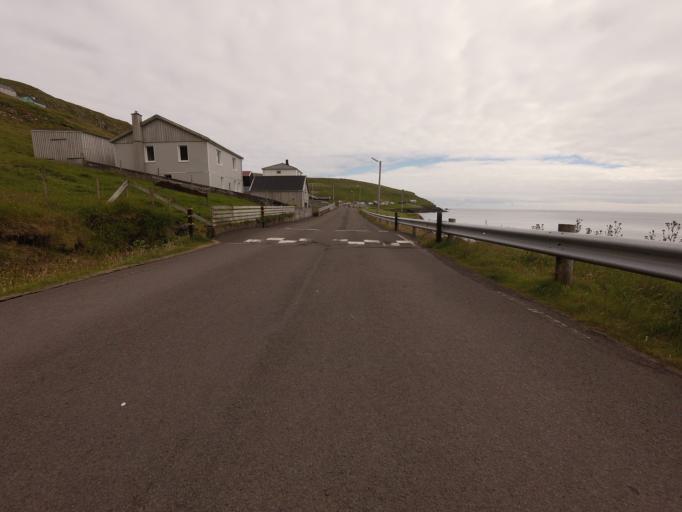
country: FO
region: Suduroy
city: Vagur
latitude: 61.4058
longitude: -6.7234
